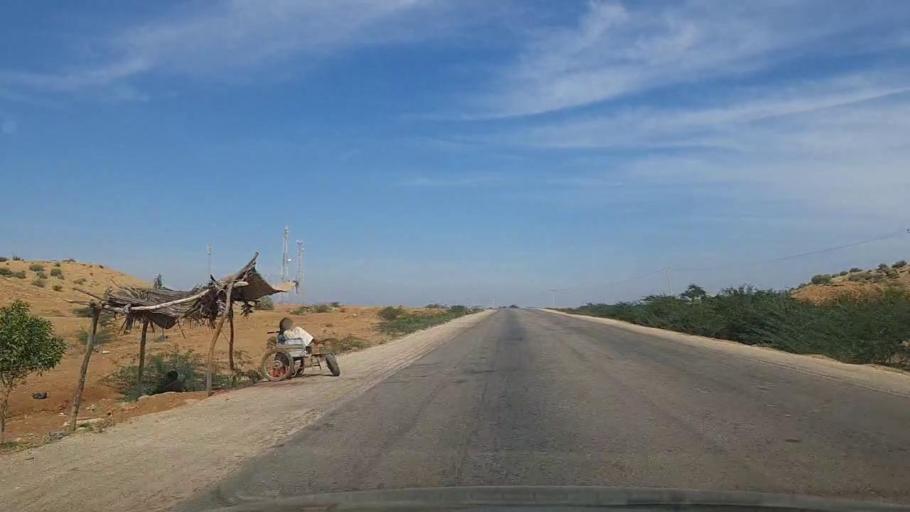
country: PK
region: Sindh
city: Bulri
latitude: 25.0481
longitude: 68.2443
